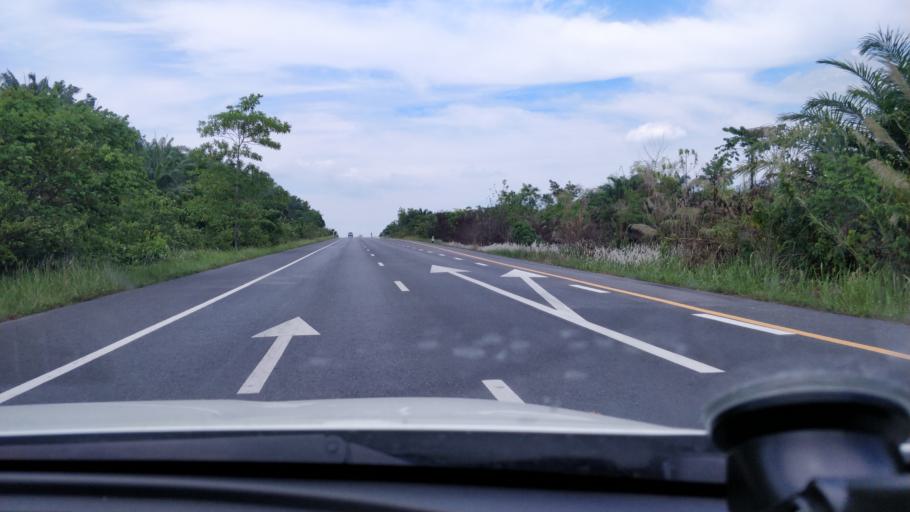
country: TH
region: Krabi
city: Plai Phraya
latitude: 8.4687
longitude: 98.8656
